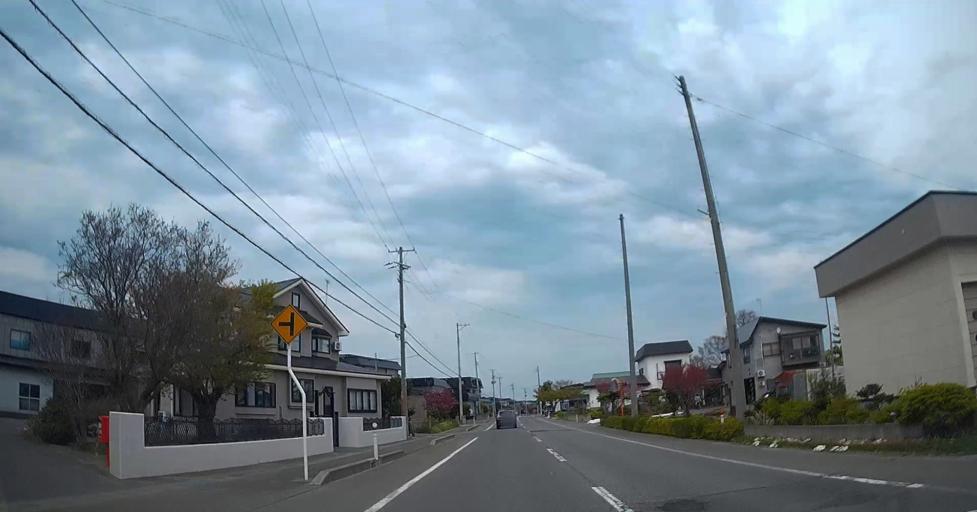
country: JP
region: Aomori
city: Shimokizukuri
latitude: 40.9999
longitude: 140.3440
